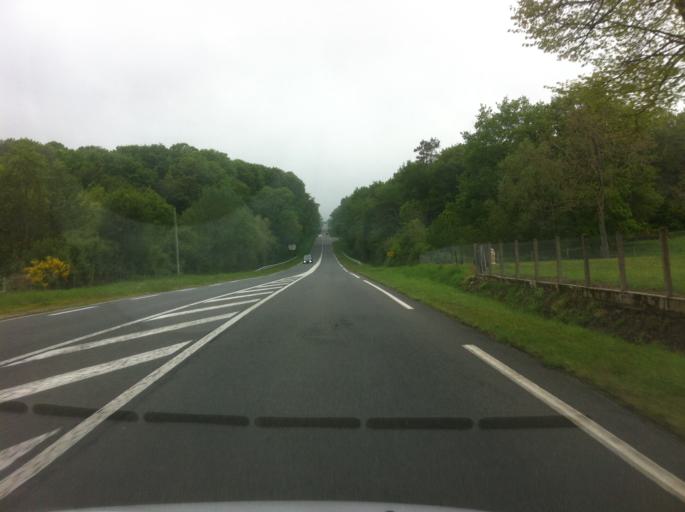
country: FR
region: Auvergne
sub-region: Departement de l'Allier
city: Chantelle
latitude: 46.3231
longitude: 3.0851
